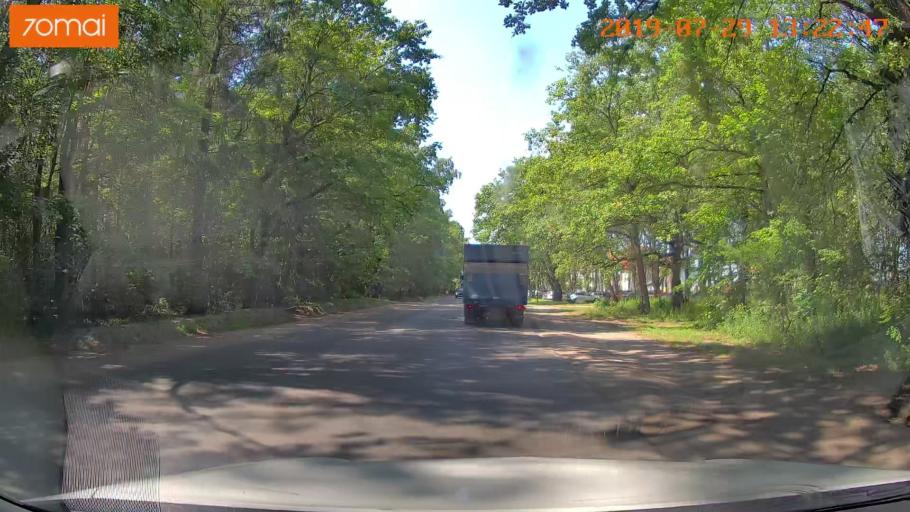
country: RU
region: Kaliningrad
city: Vzmorye
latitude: 54.7149
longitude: 20.3653
